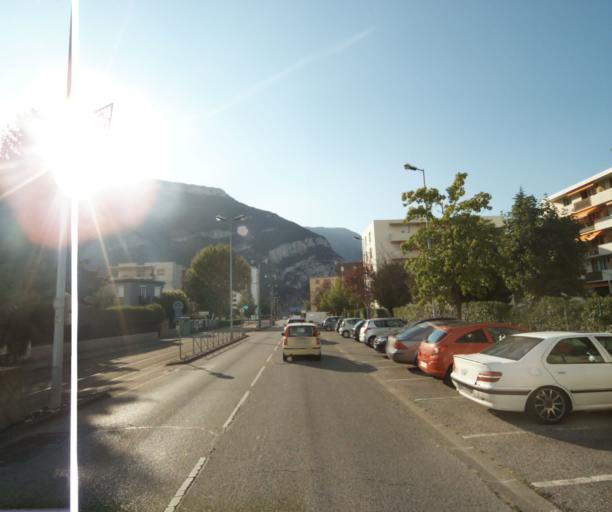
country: FR
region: Rhone-Alpes
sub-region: Departement de l'Isere
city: Fontaine
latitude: 45.1943
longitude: 5.6792
